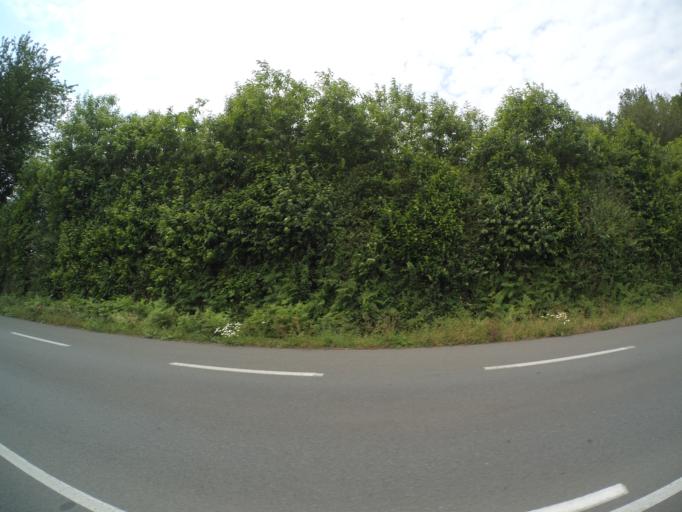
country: FR
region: Pays de la Loire
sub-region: Departement de la Vendee
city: Chavagnes-en-Paillers
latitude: 46.8853
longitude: -1.2147
